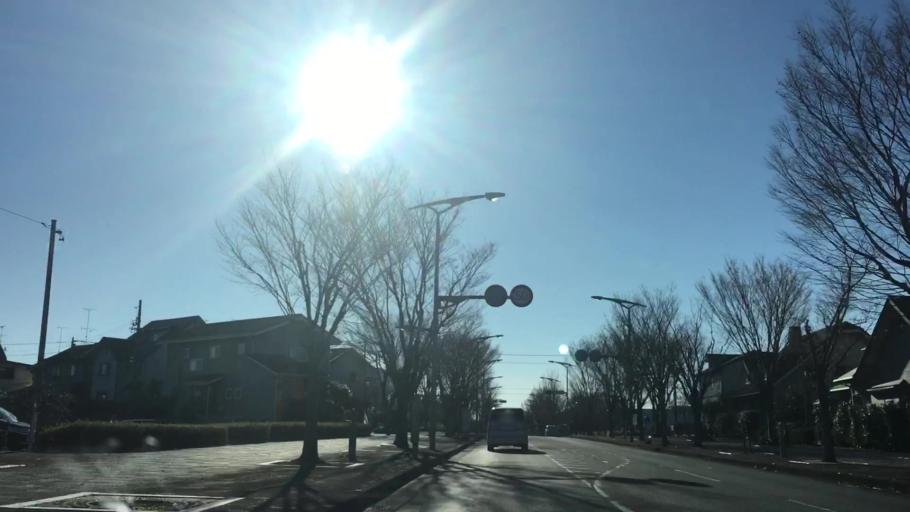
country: JP
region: Shizuoka
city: Hamakita
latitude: 34.8152
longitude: 137.7419
